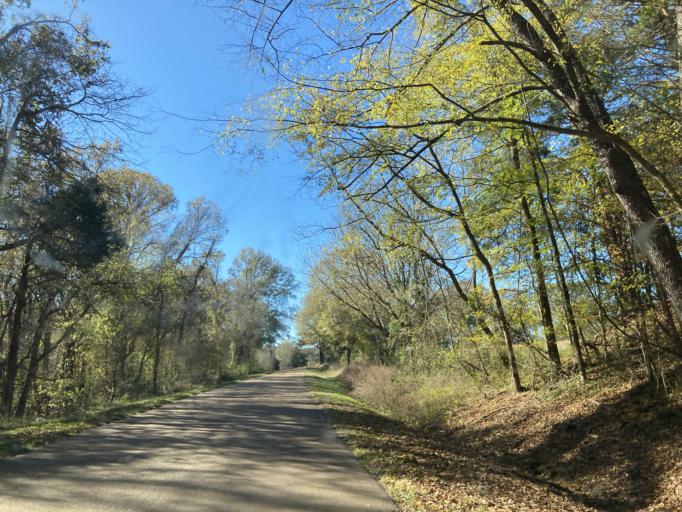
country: US
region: Mississippi
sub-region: Hinds County
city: Lynchburg
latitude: 32.5784
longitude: -90.5704
